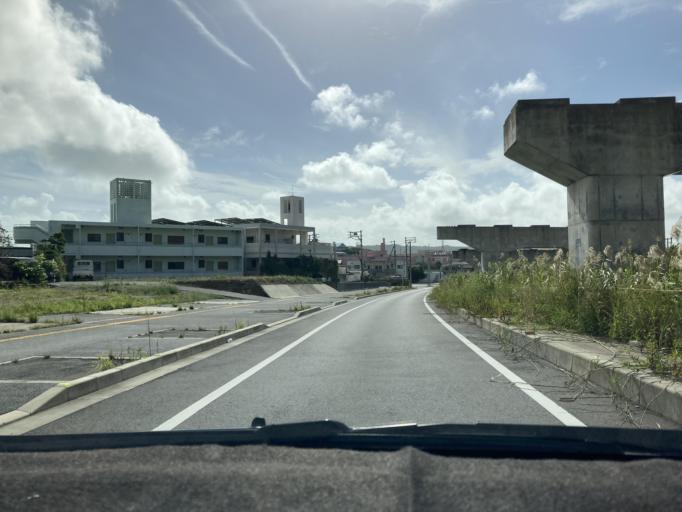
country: JP
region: Okinawa
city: Naha-shi
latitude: 26.2053
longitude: 127.7332
